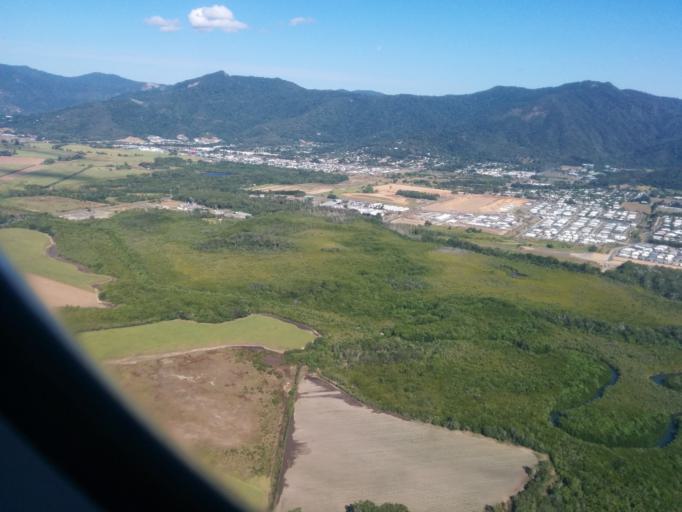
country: AU
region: Queensland
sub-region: Cairns
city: Yorkeys Knob
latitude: -16.8178
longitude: 145.7219
